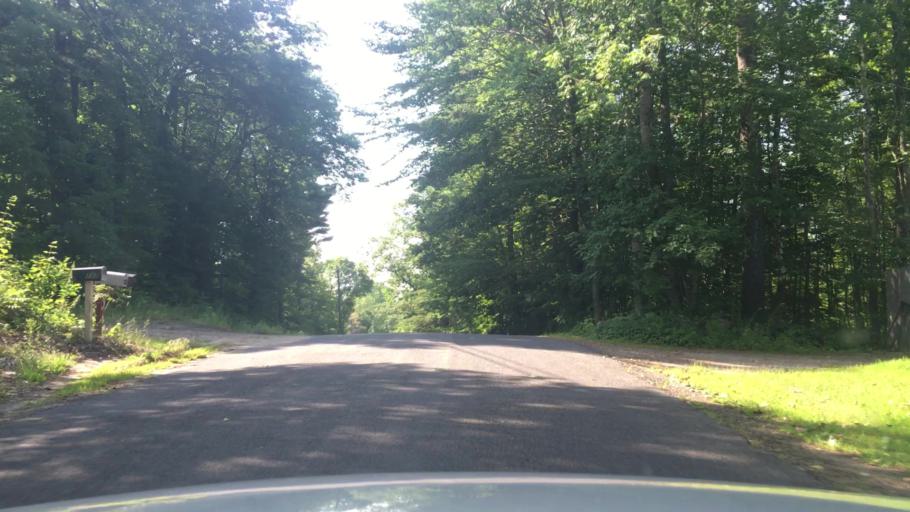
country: US
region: Maine
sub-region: Androscoggin County
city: Greene
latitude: 44.2339
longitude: -70.1059
